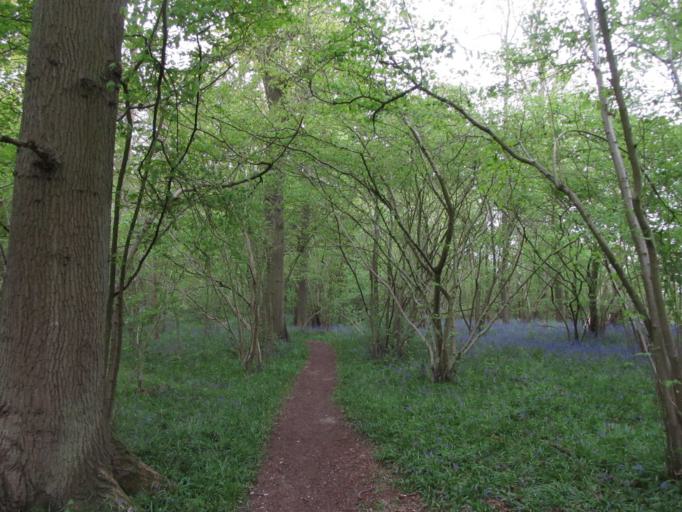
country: GB
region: England
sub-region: Royal Borough of Windsor and Maidenhead
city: Bisham
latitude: 51.5415
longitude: -0.7636
